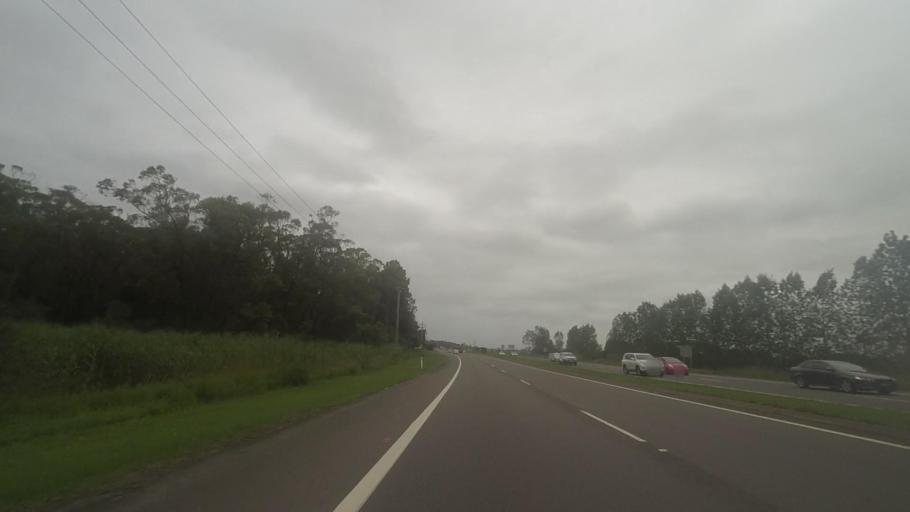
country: AU
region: New South Wales
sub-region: Port Stephens Shire
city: Raymond Terrace
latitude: -32.7998
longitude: 151.7169
